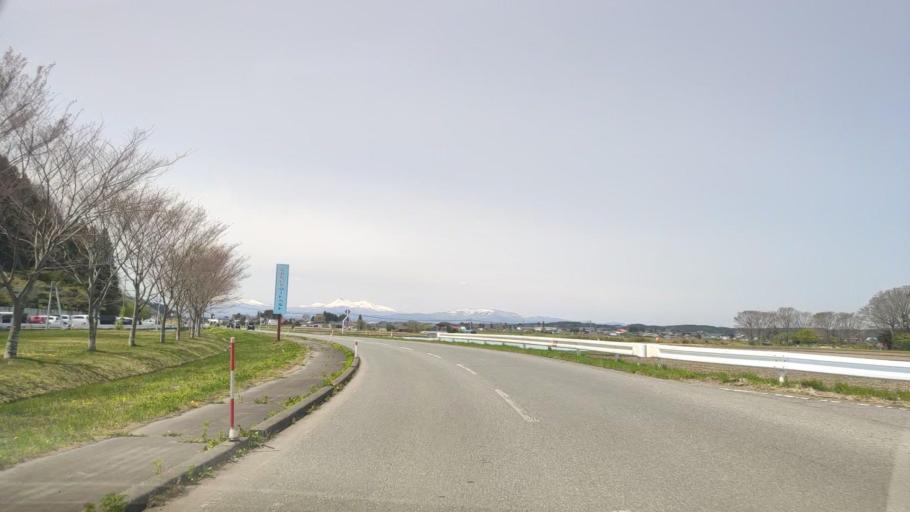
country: JP
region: Aomori
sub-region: Misawa Shi
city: Inuotose
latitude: 40.5940
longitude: 141.3411
